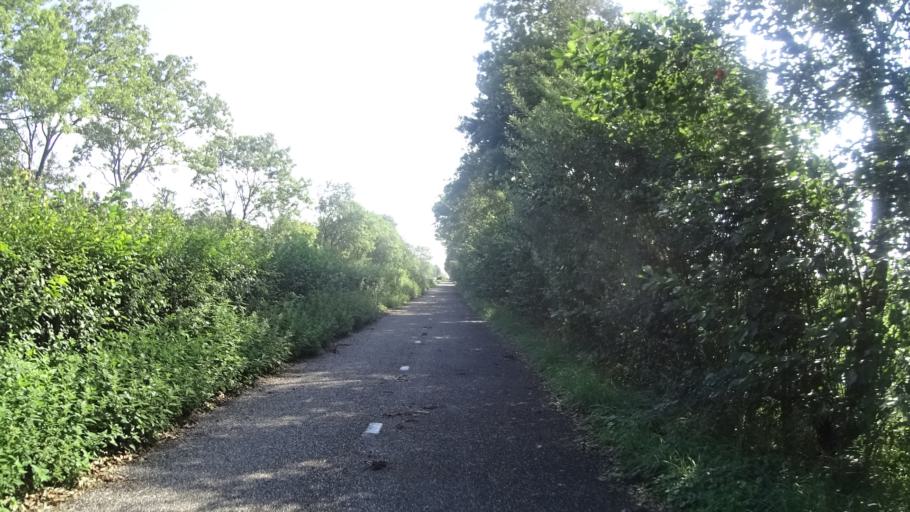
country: NL
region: Friesland
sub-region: Gemeente Franekeradeel
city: Tzum
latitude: 53.1901
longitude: 5.5750
